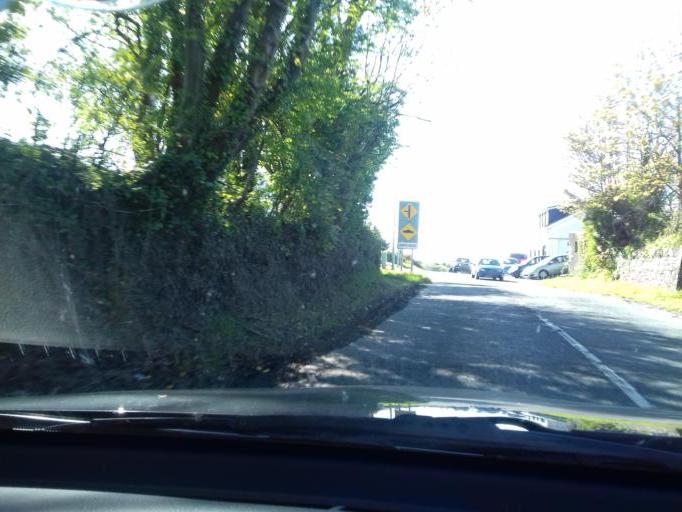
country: IE
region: Munster
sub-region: Waterford
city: Waterford
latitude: 52.2806
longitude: -7.1445
